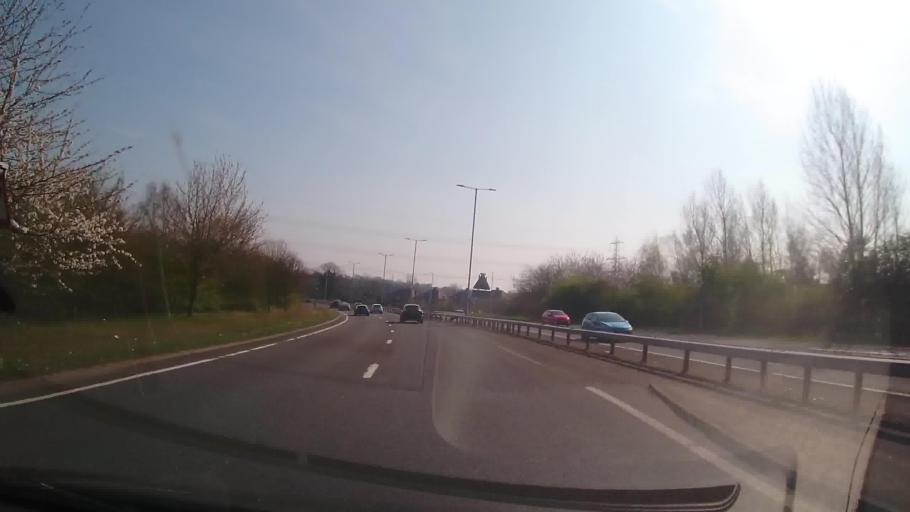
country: GB
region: England
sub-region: Leicestershire
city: Glenfield
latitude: 52.6603
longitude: -1.2031
